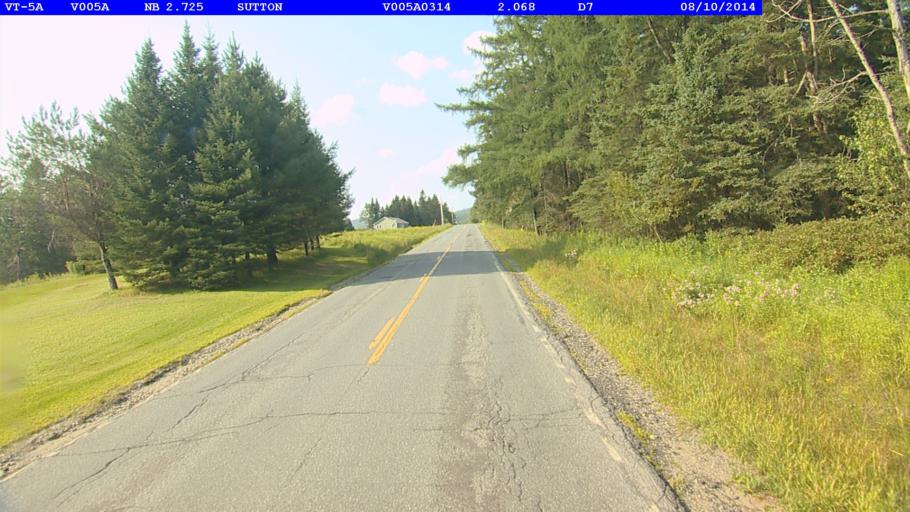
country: US
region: Vermont
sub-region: Caledonia County
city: Lyndonville
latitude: 44.6768
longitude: -71.9954
